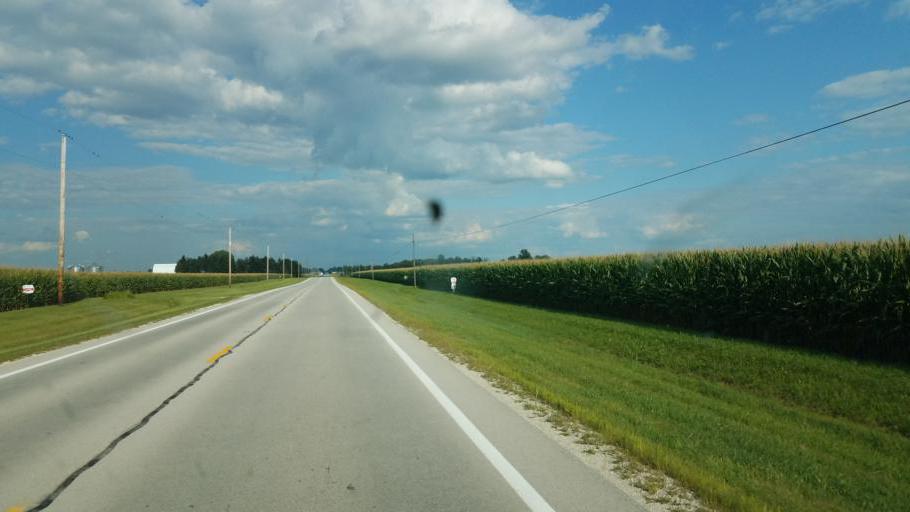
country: US
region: Ohio
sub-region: Wood County
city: Pemberville
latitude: 41.3413
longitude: -83.4035
